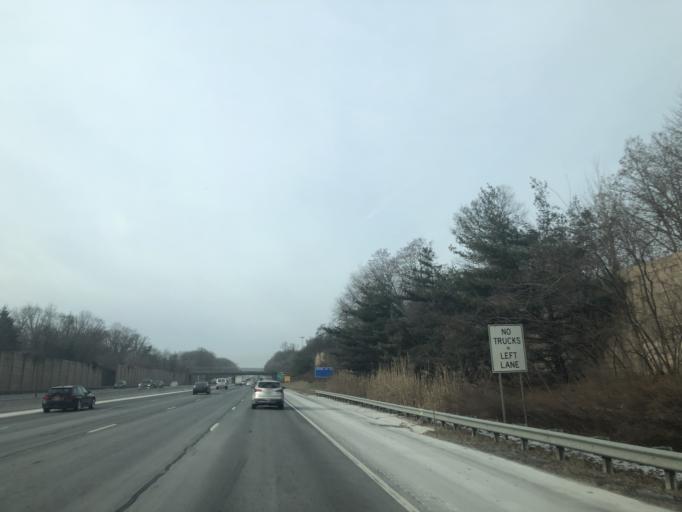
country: US
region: New Jersey
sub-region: Morris County
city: Rockaway
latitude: 40.9113
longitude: -74.5228
